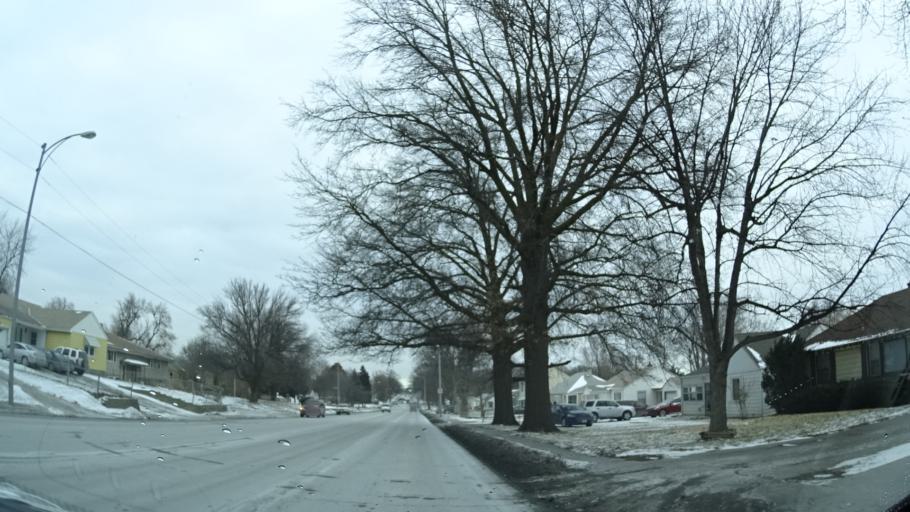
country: US
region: Nebraska
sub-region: Douglas County
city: Omaha
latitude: 41.2295
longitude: -95.9758
